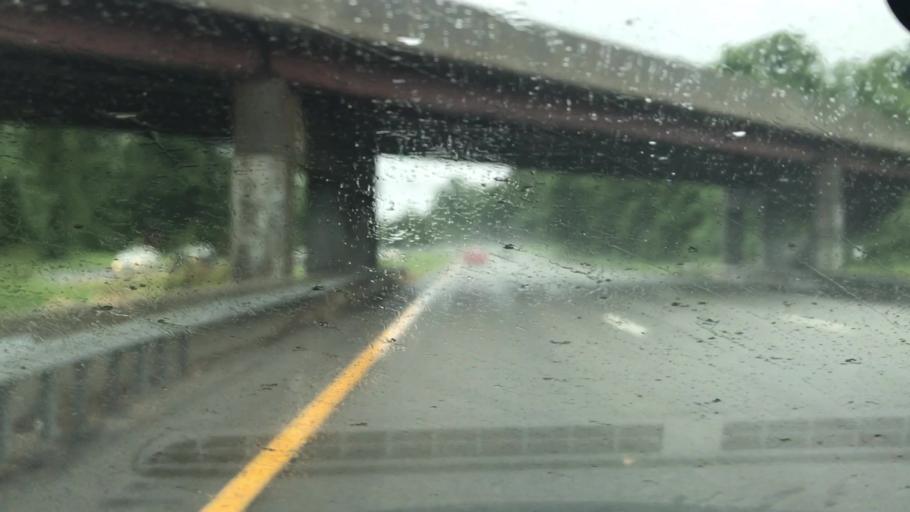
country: US
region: New York
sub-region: Westchester County
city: Briarcliff Manor
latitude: 41.1994
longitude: -73.8072
